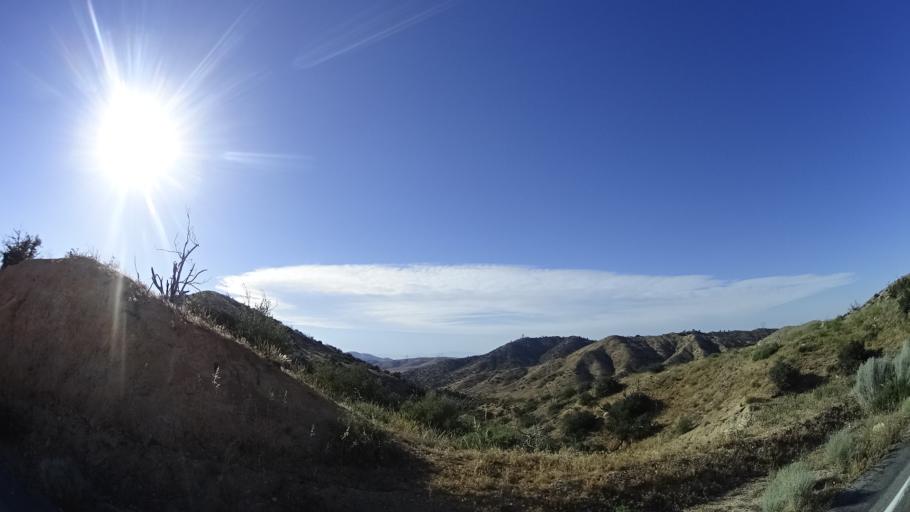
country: US
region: California
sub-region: Los Angeles County
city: Vincent
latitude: 34.4686
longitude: -118.0748
